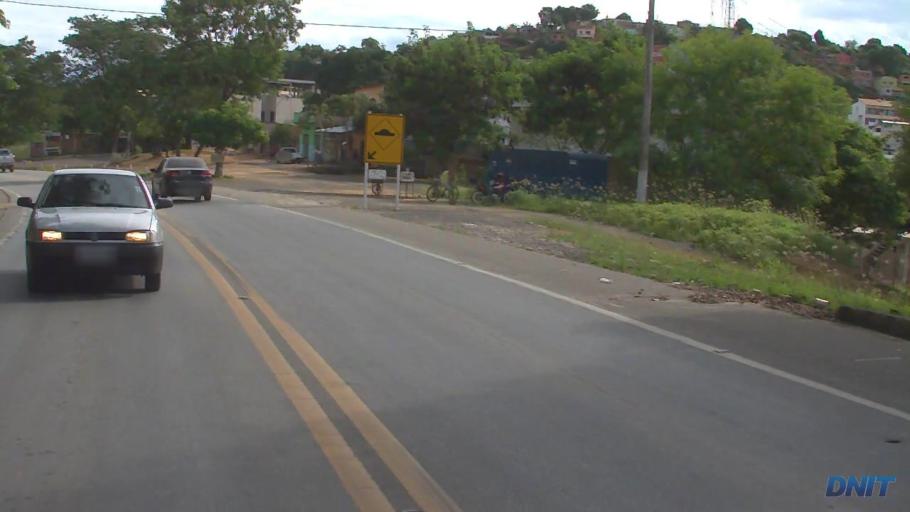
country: BR
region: Minas Gerais
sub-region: Belo Oriente
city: Belo Oriente
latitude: -19.2303
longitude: -42.3270
